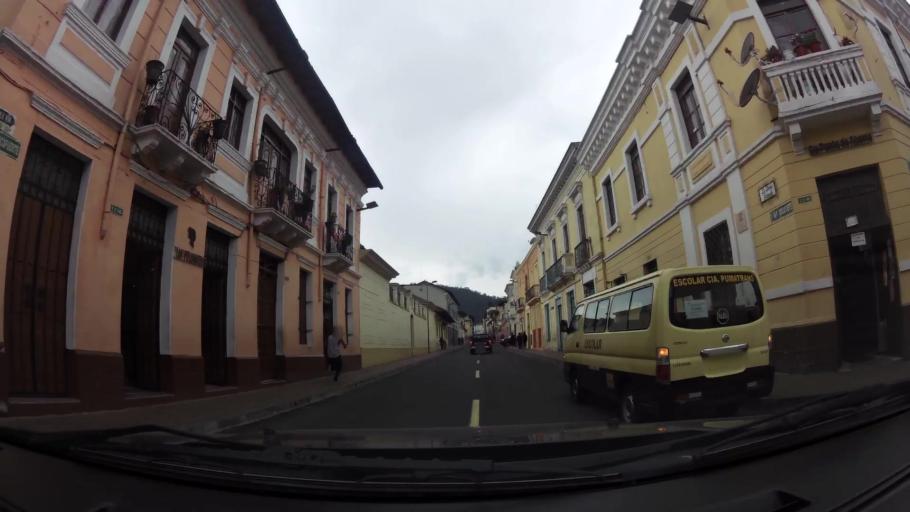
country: EC
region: Pichincha
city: Quito
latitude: -0.2268
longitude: -78.5107
